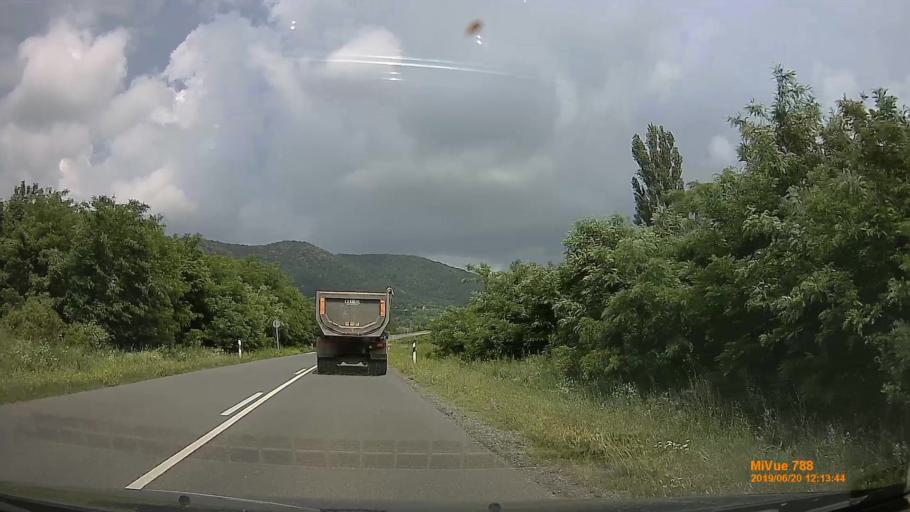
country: HU
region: Baranya
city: Hosszuheteny
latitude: 46.1611
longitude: 18.3423
